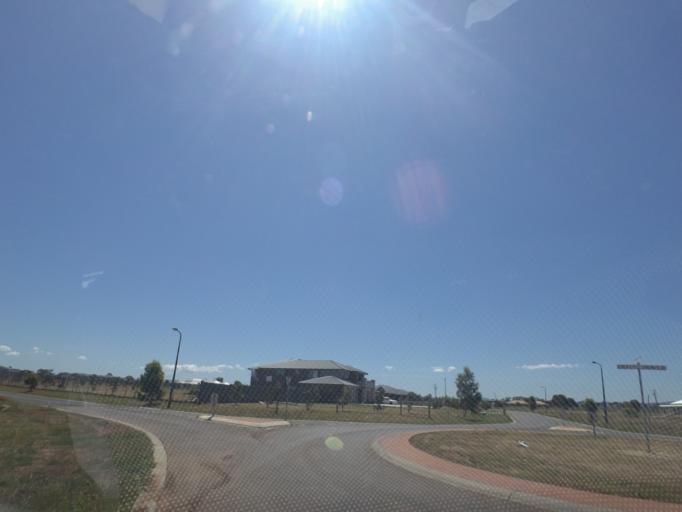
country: AU
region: Victoria
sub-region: Melton
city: Brookfield
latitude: -37.6977
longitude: 144.5099
